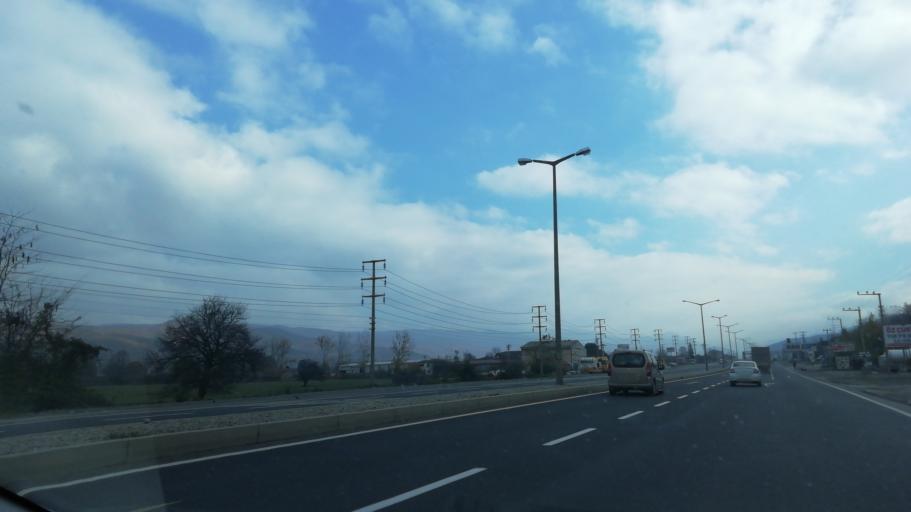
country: TR
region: Duzce
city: Kaynasli
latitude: 40.7779
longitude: 31.2932
